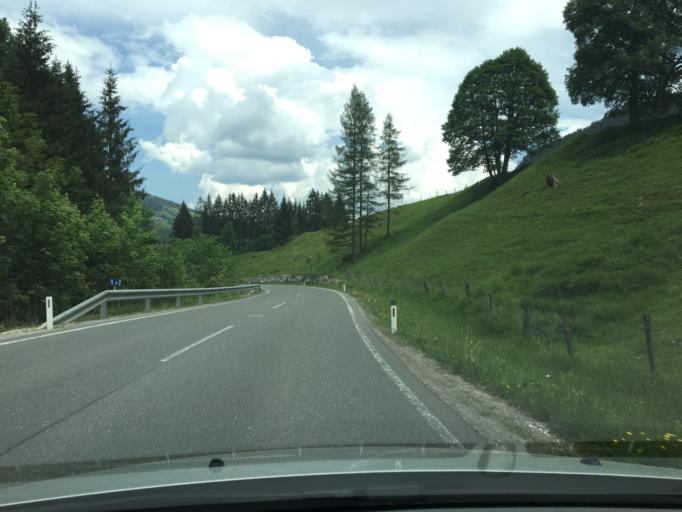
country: AT
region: Salzburg
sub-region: Politischer Bezirk Sankt Johann im Pongau
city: Kleinarl
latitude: 47.2900
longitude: 13.3077
